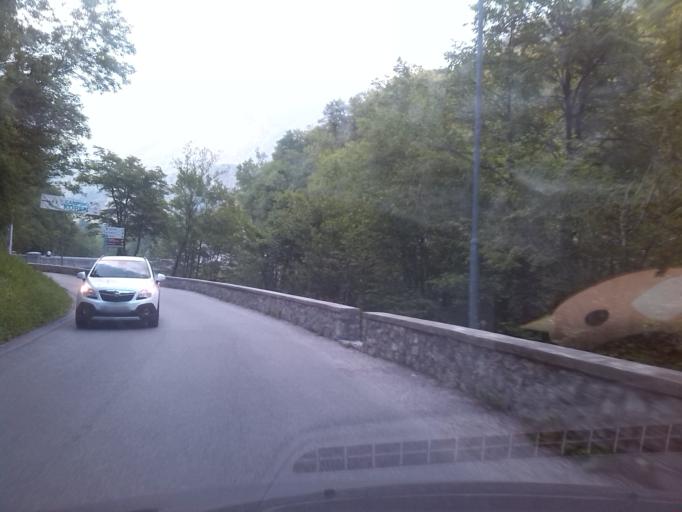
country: SI
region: Kobarid
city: Kobarid
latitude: 46.2474
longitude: 13.5861
